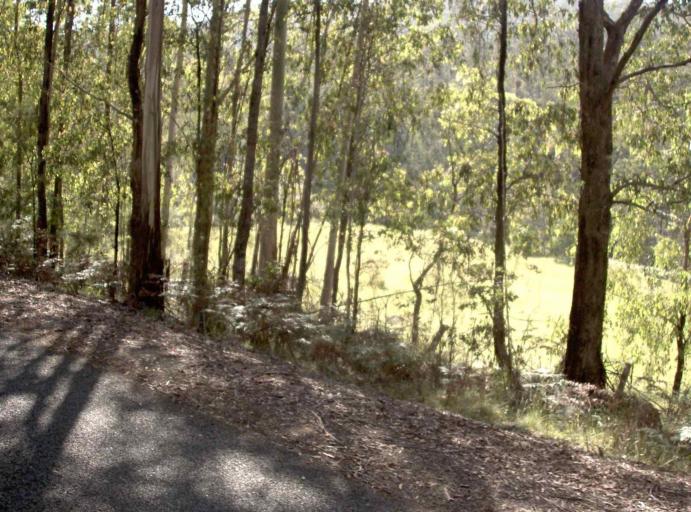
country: AU
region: New South Wales
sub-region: Bombala
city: Bombala
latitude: -37.3807
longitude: 148.6756
